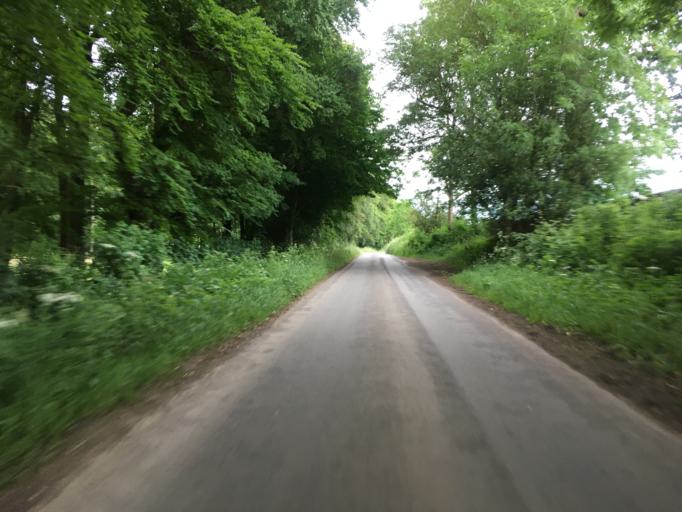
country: GB
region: England
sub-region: Wiltshire
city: Luckington
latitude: 51.5725
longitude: -2.2723
